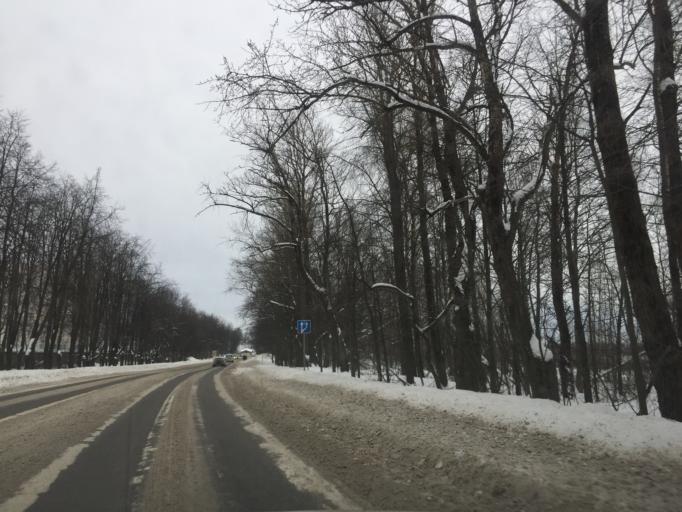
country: RU
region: Leningrad
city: Yanino Vtoroye
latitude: 59.9431
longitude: 30.6056
